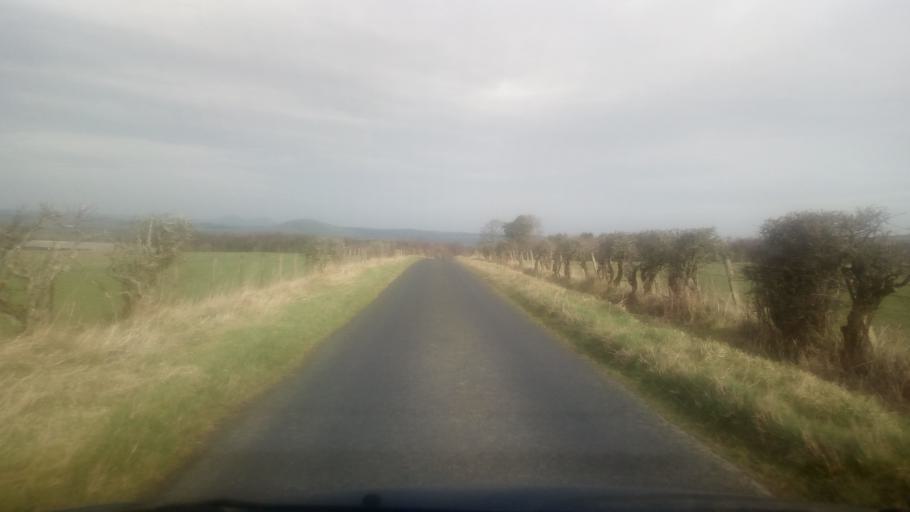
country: GB
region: Scotland
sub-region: The Scottish Borders
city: Hawick
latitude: 55.4214
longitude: -2.7029
